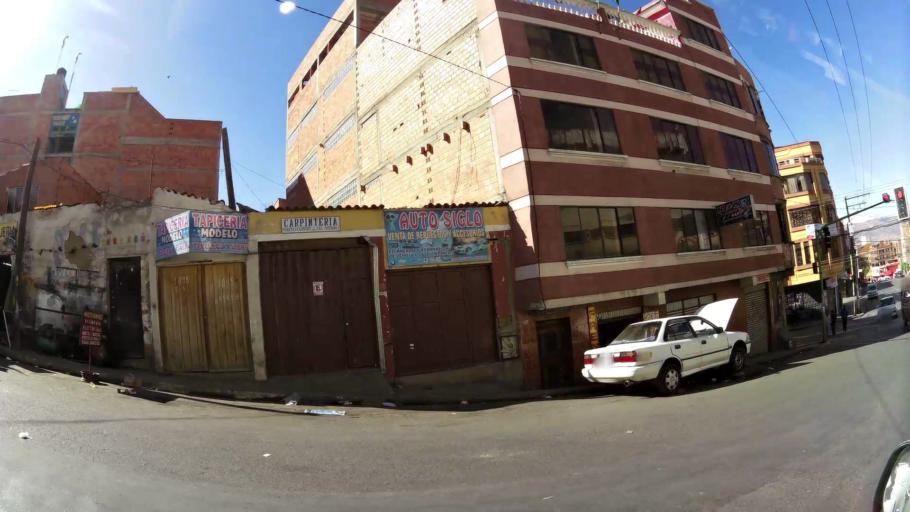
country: BO
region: La Paz
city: La Paz
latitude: -16.5116
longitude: -68.1412
